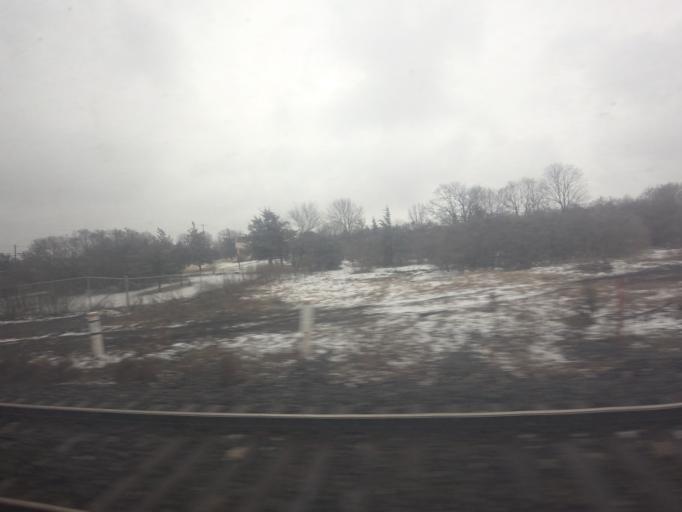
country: CA
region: Ontario
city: Belleville
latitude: 44.2041
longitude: -77.2362
